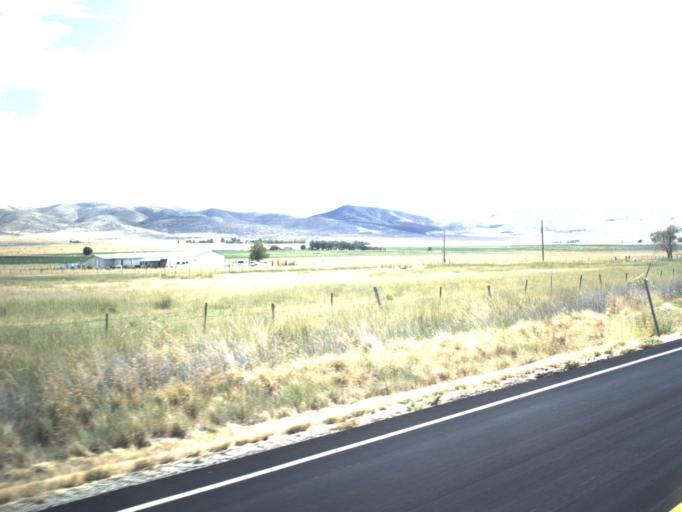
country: US
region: Utah
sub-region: Box Elder County
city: Garland
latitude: 41.7680
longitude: -112.4351
